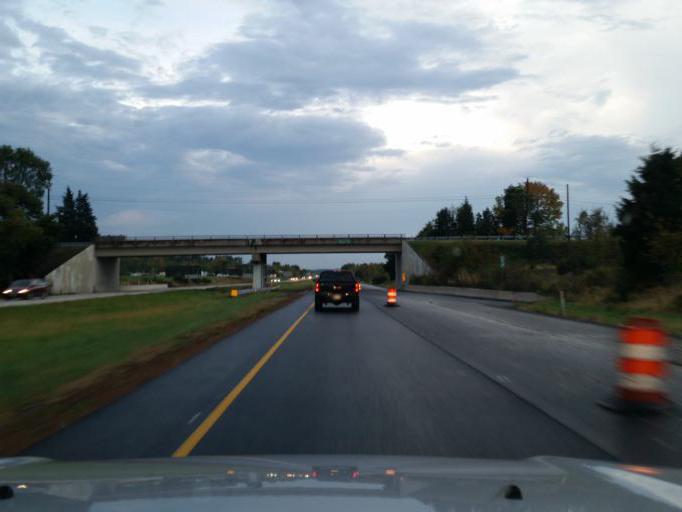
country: US
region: Maryland
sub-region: Frederick County
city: Emmitsburg
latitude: 39.7259
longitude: -77.3037
